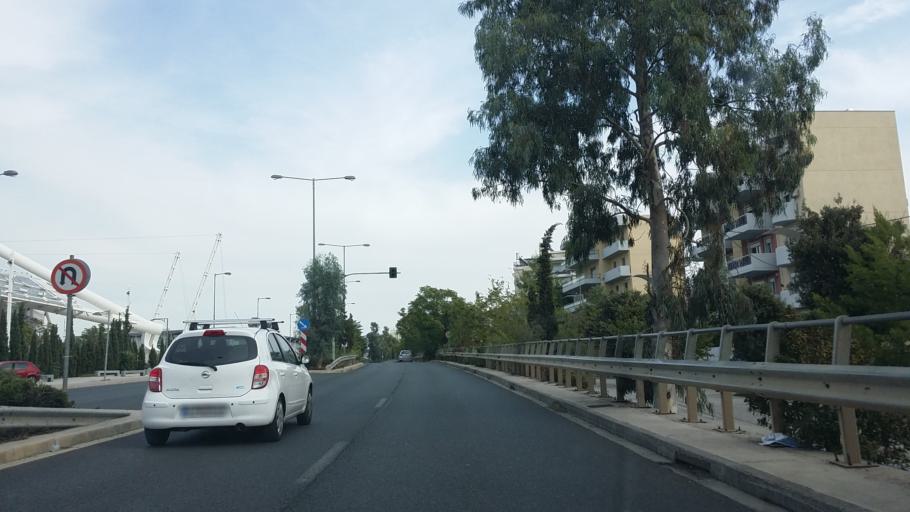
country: GR
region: Attica
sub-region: Nomarchia Athinas
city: Filothei
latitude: 38.0345
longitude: 23.7841
